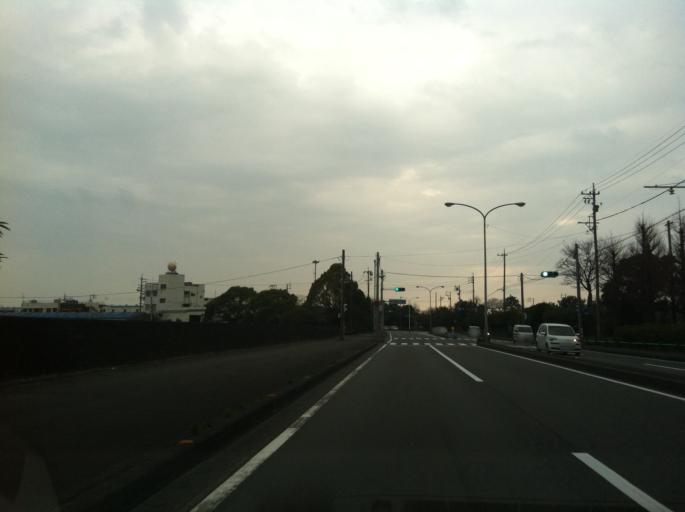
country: JP
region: Shizuoka
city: Shizuoka-shi
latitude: 35.0433
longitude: 138.5050
